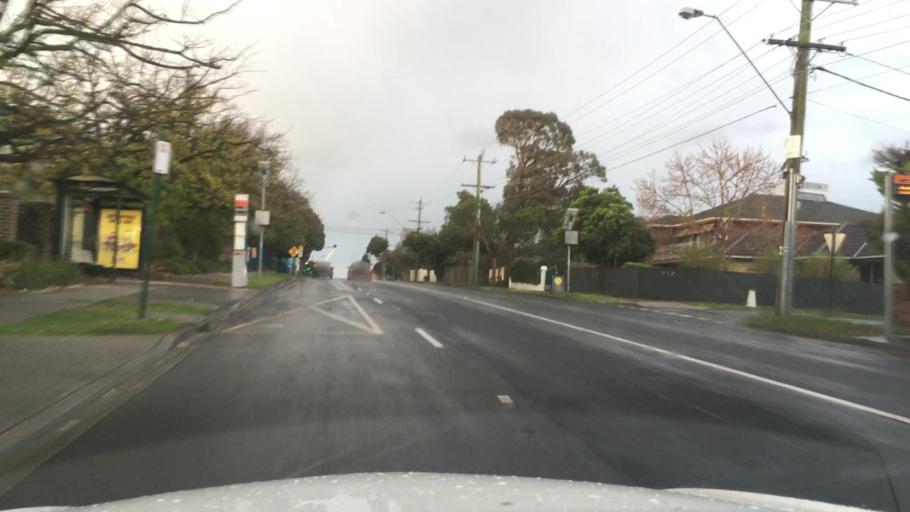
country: AU
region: Victoria
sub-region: Whitehorse
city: Box Hill South
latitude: -37.8341
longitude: 145.1208
